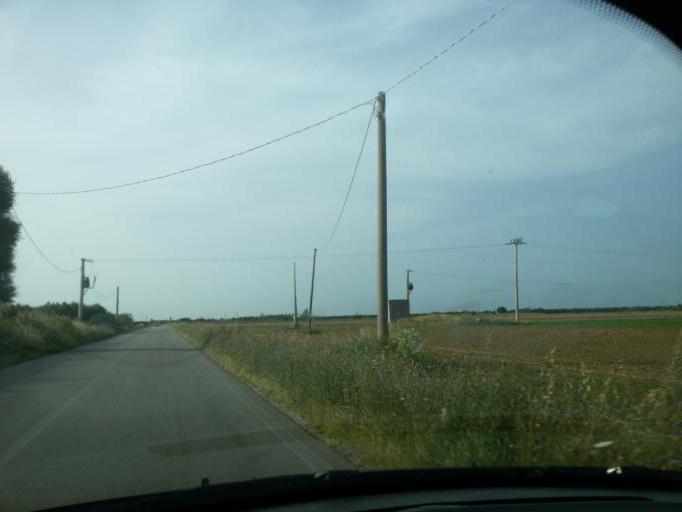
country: IT
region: Apulia
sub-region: Provincia di Brindisi
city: San Pancrazio Salentino
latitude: 40.3900
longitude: 17.8355
